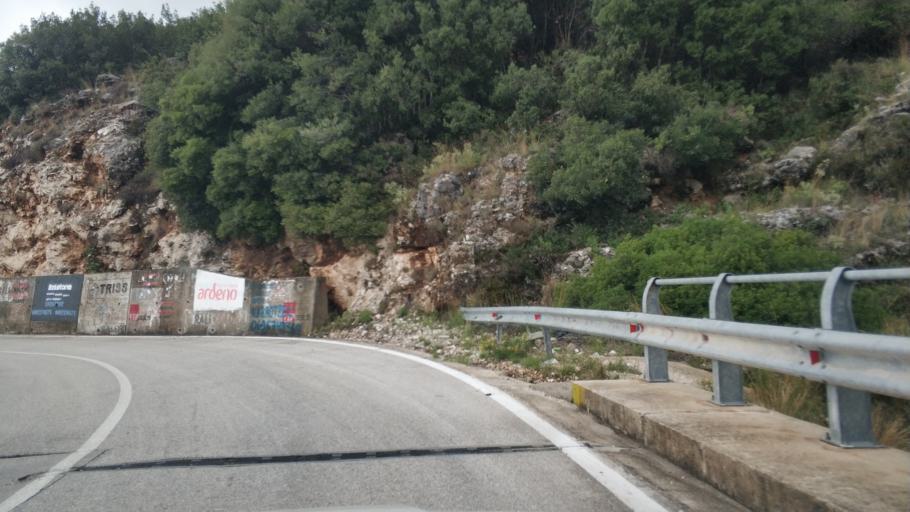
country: AL
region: Vlore
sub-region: Rrethi i Vlores
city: Vranisht
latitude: 40.1751
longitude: 19.6068
